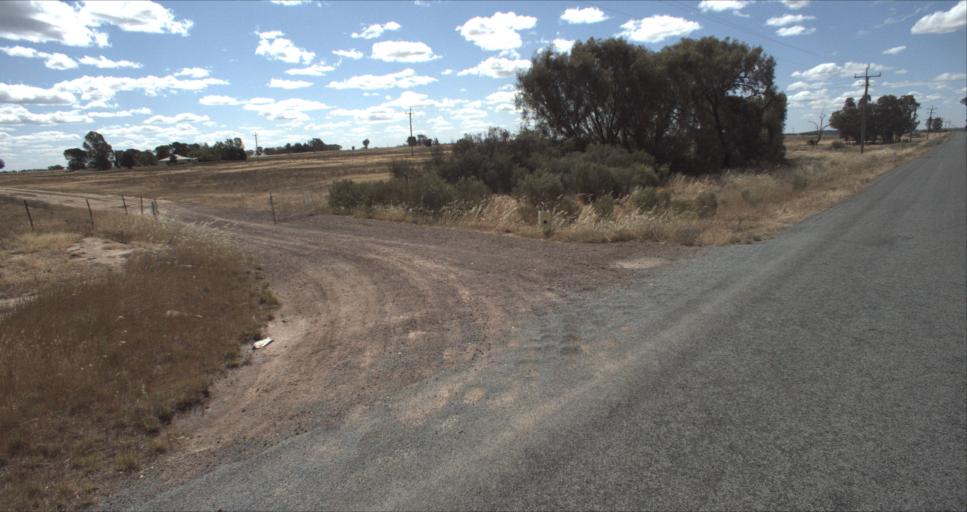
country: AU
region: New South Wales
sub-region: Leeton
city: Leeton
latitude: -34.4879
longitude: 146.2478
